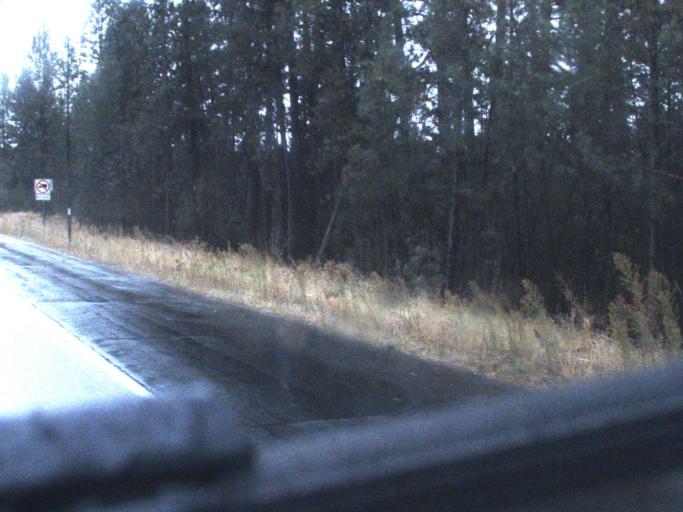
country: US
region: Washington
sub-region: Spokane County
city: Spokane
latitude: 47.5756
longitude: -117.4020
